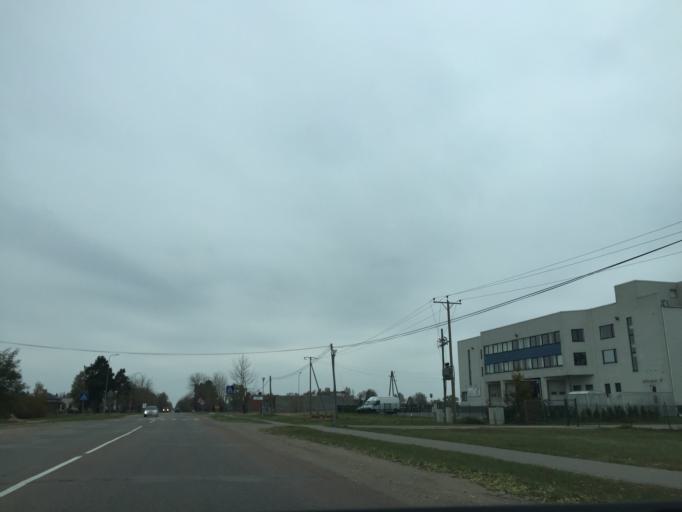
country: LV
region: Marupe
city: Marupe
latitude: 56.8886
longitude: 24.0719
